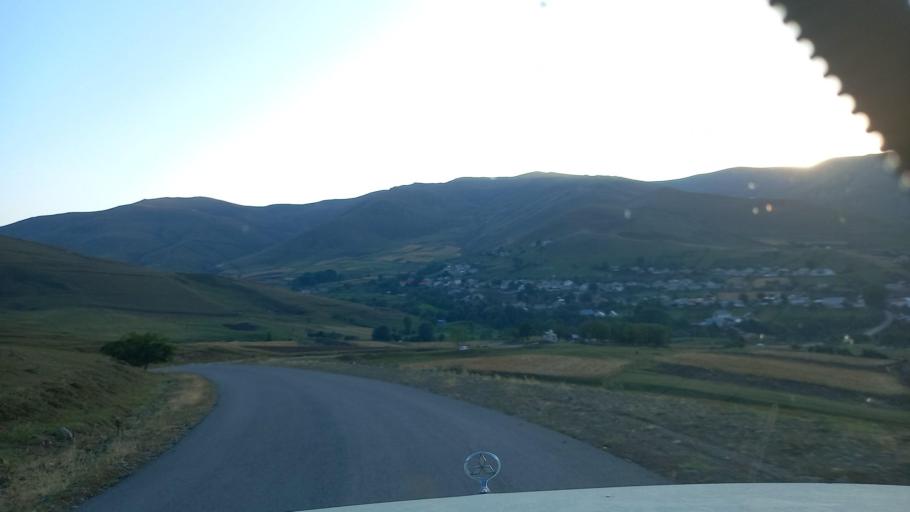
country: AZ
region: Tovuz
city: Cobansignaq
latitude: 40.6842
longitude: 45.7717
